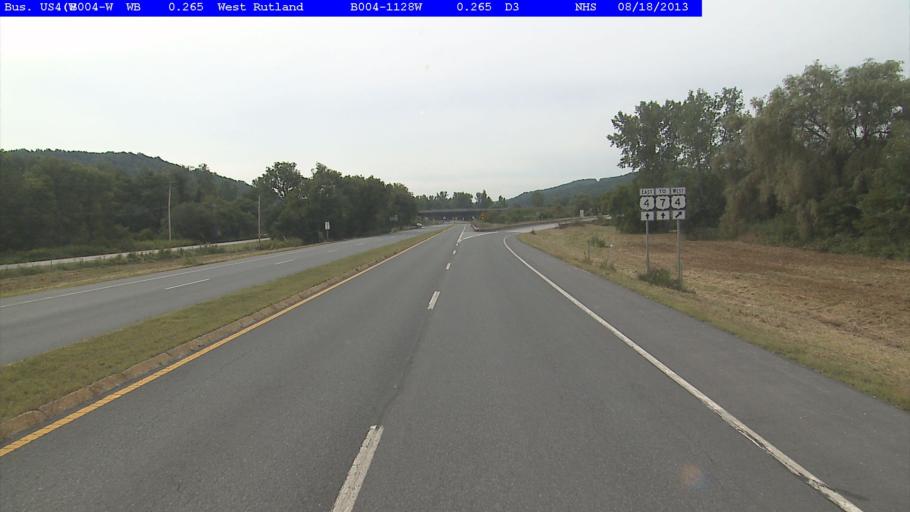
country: US
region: Vermont
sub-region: Rutland County
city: West Rutland
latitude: 43.5913
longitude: -73.0408
